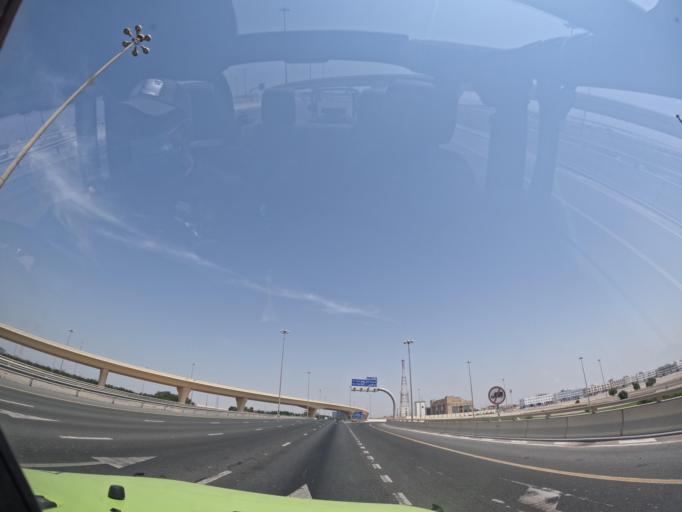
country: AE
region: Abu Dhabi
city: Abu Dhabi
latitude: 24.3091
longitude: 54.6015
